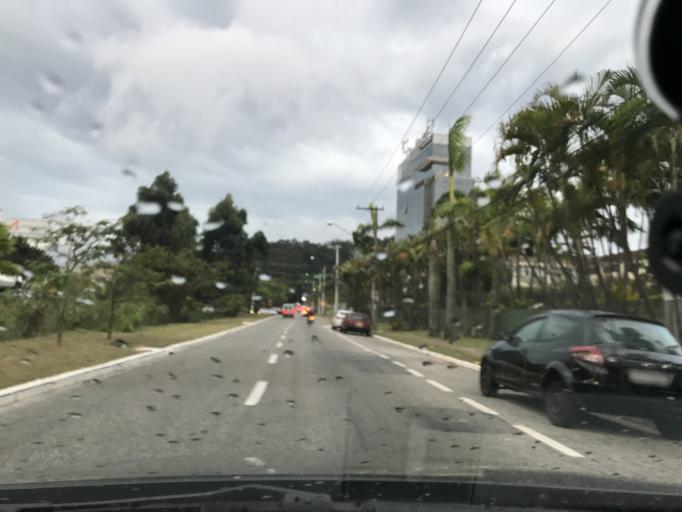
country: BR
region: Sao Paulo
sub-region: Carapicuiba
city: Carapicuiba
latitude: -23.4981
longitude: -46.8305
